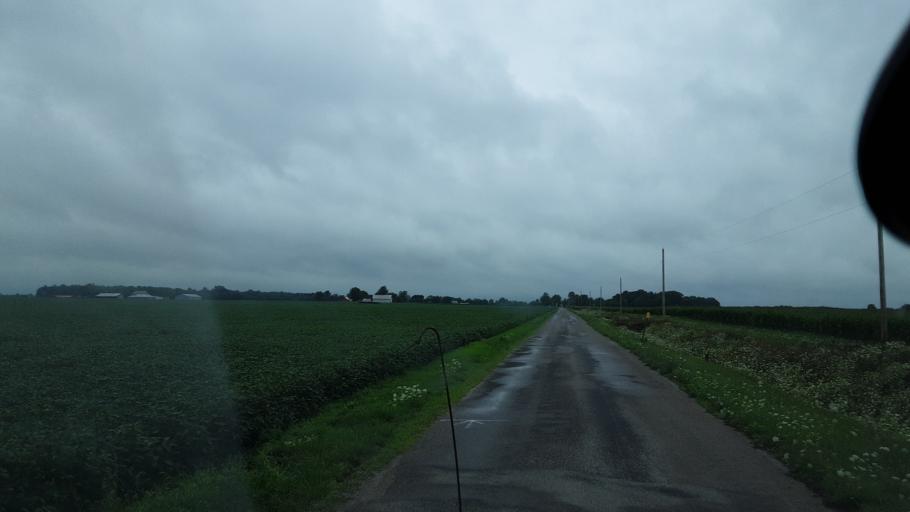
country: US
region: Ohio
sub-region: Van Wert County
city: Convoy
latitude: 40.8297
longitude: -84.7913
